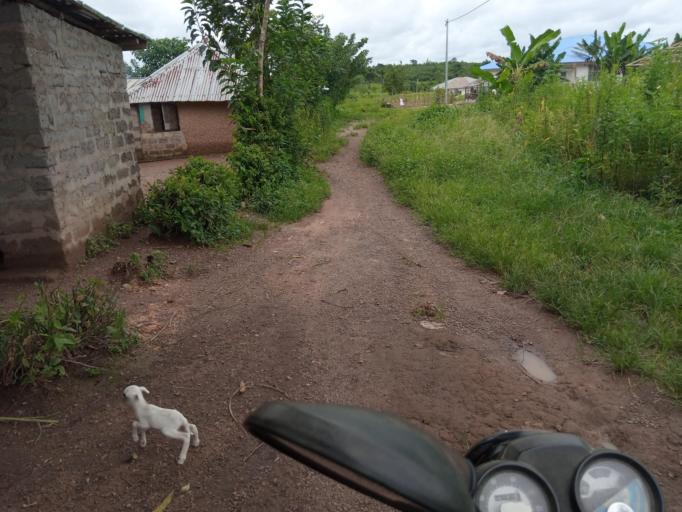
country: SL
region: Southern Province
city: Largo
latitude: 8.1920
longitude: -12.0608
